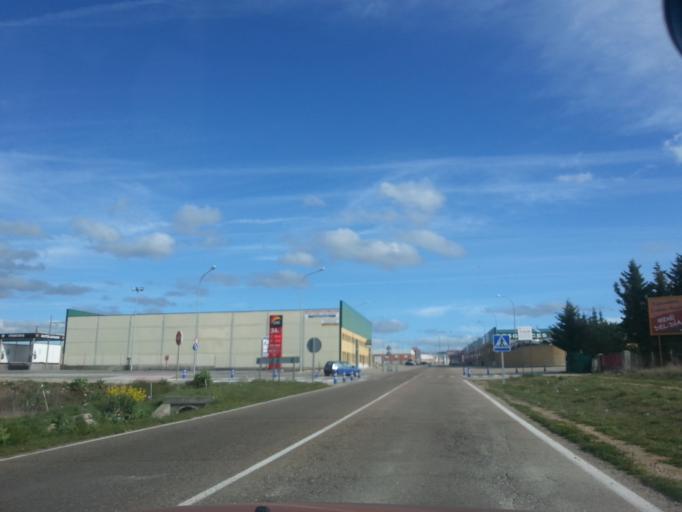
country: ES
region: Castille and Leon
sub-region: Provincia de Salamanca
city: Villares de la Reina
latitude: 40.9968
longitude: -5.6508
